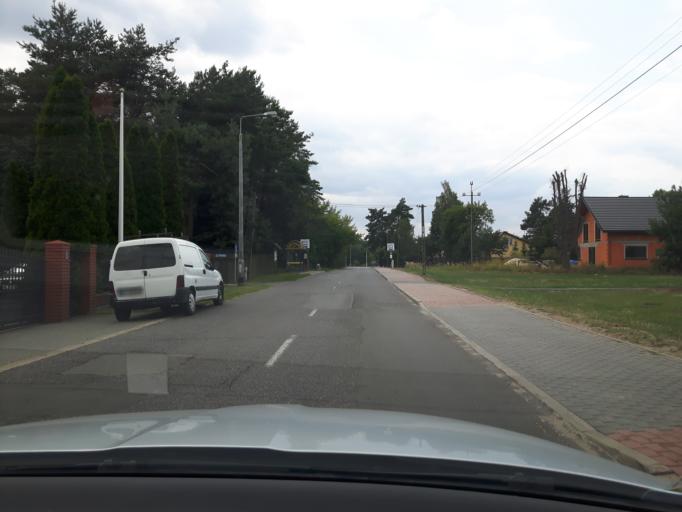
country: PL
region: Masovian Voivodeship
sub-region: Powiat legionowski
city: Wieliszew
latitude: 52.4705
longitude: 20.9279
